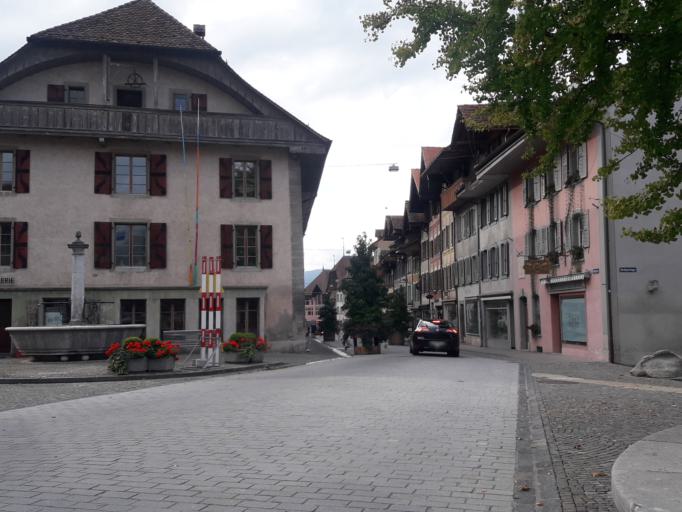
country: CH
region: Bern
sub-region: Biel/Bienne District
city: Meinisberg
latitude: 47.1396
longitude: 7.3738
